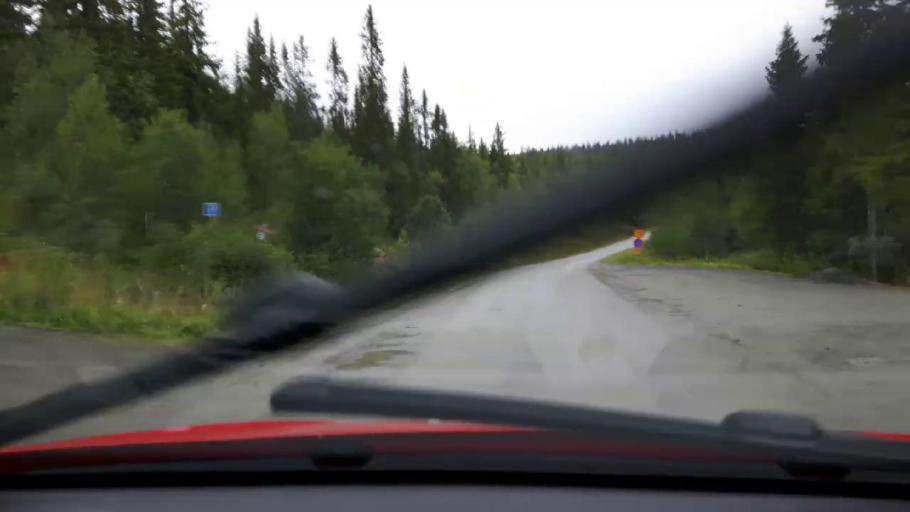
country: SE
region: Jaemtland
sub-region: Are Kommun
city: Are
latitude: 63.3936
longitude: 13.1445
